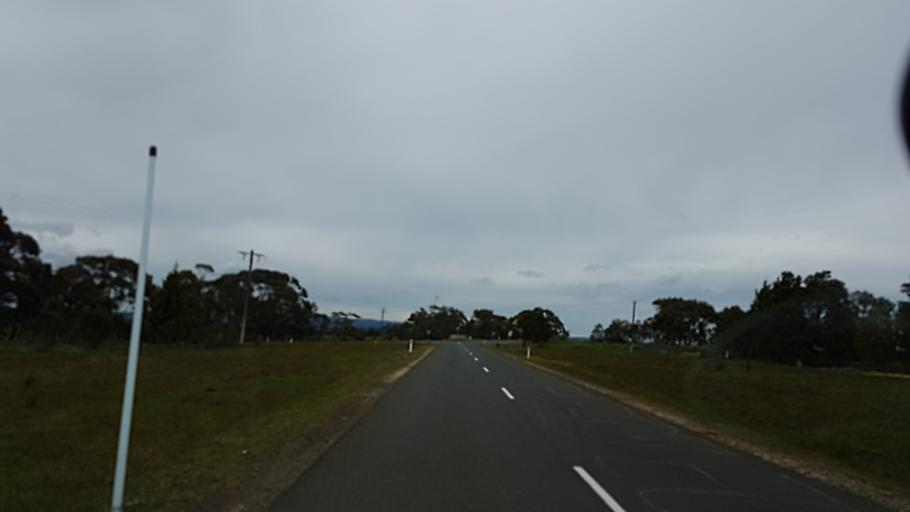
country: AU
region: Victoria
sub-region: Moorabool
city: Bacchus Marsh
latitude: -37.6253
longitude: 144.2096
